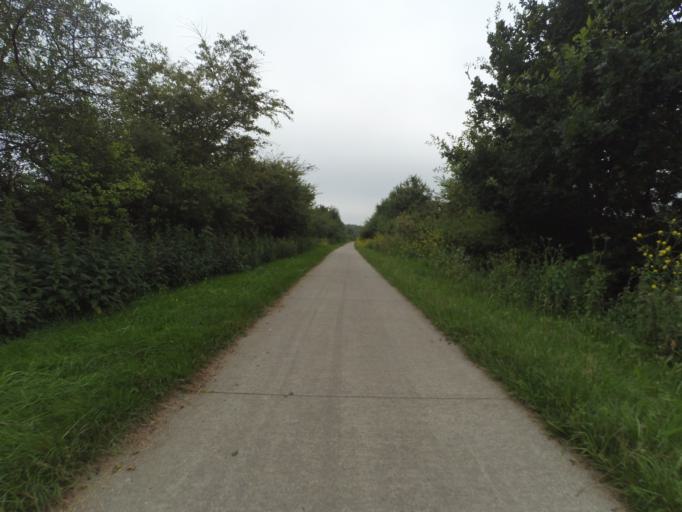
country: NL
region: Flevoland
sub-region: Gemeente Almere
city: Almere Stad
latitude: 52.4224
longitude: 5.2792
